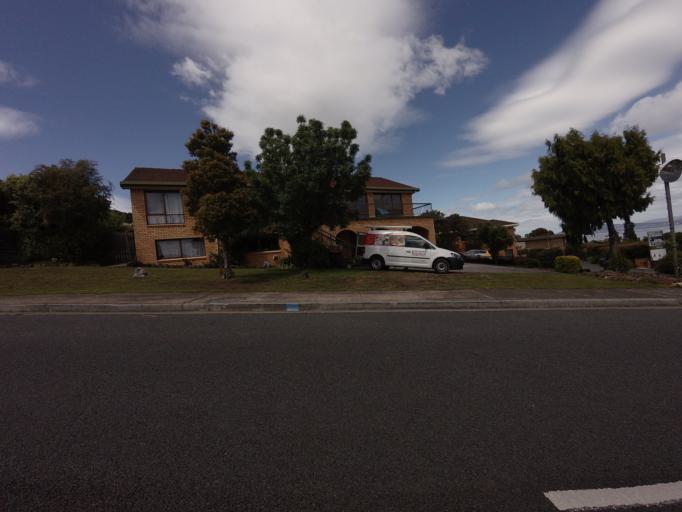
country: AU
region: Tasmania
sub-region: Clarence
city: Howrah
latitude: -42.8879
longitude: 147.4106
